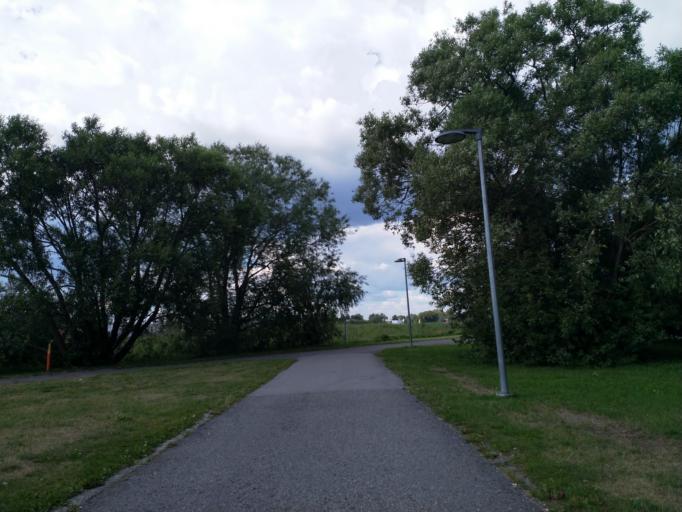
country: EE
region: Paernumaa
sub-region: Paernu linn
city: Parnu
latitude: 58.3833
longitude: 24.4838
